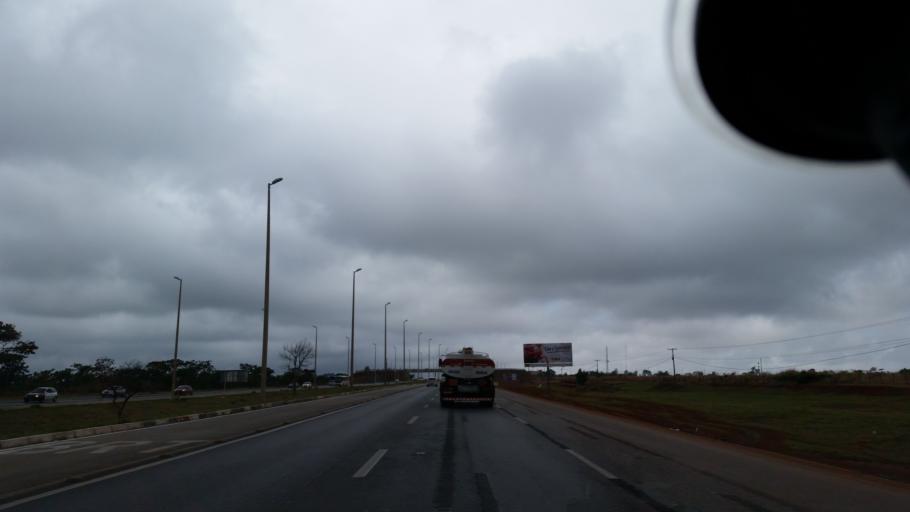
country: BR
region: Federal District
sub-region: Brasilia
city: Brasilia
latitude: -15.9686
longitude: -47.9917
